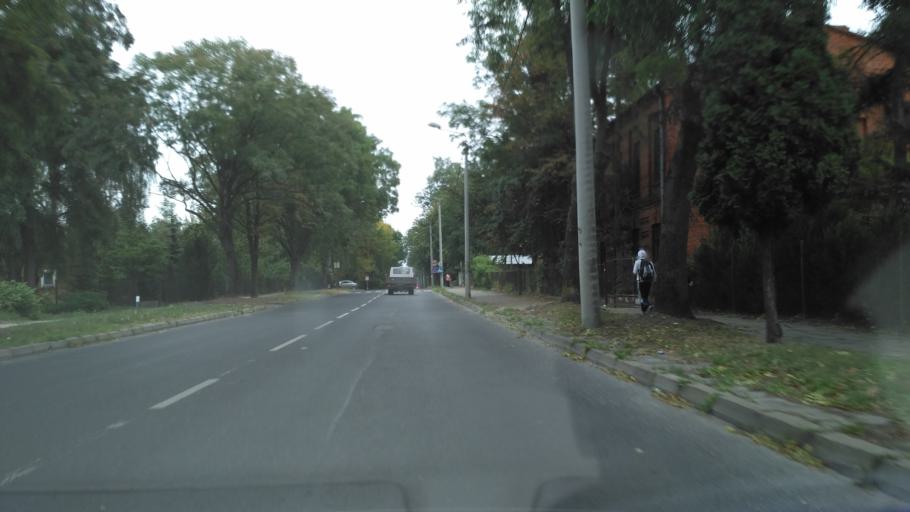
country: PL
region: Lublin Voivodeship
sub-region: Chelm
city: Chelm
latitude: 51.1432
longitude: 23.4458
